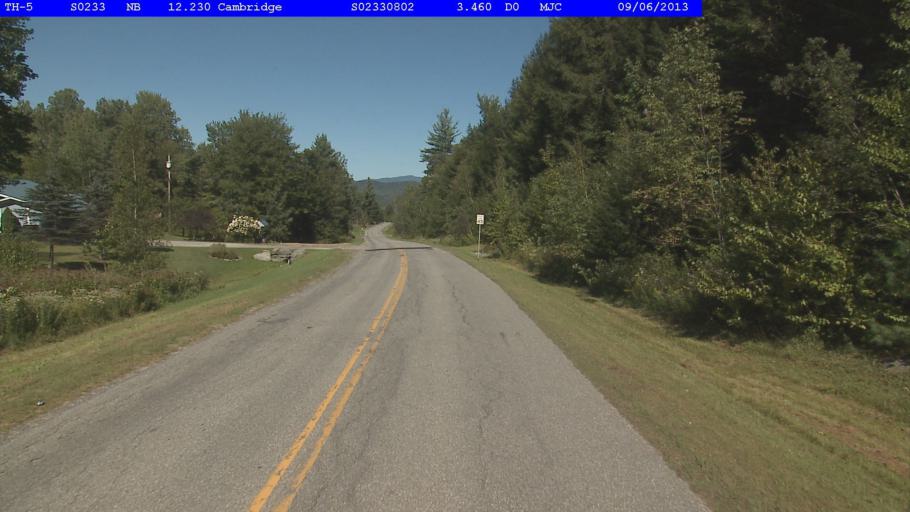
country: US
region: Vermont
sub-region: Lamoille County
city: Johnson
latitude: 44.6295
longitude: -72.8476
